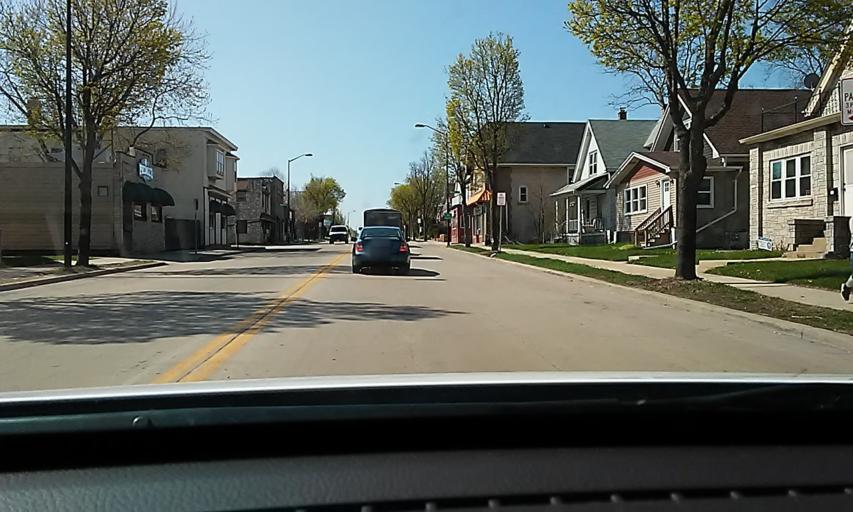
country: US
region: Wisconsin
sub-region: Milwaukee County
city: West Milwaukee
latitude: 43.0207
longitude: -87.9875
